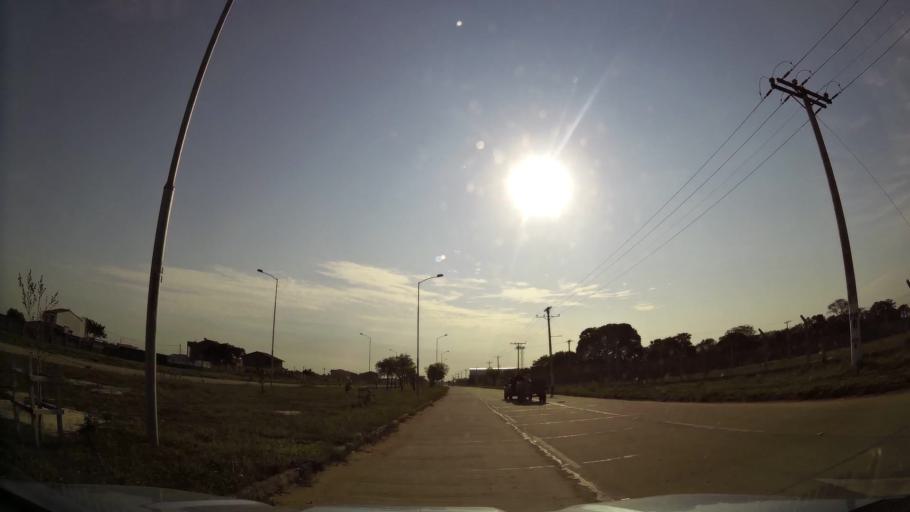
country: BO
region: Santa Cruz
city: Santa Cruz de la Sierra
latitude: -17.7023
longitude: -63.1297
